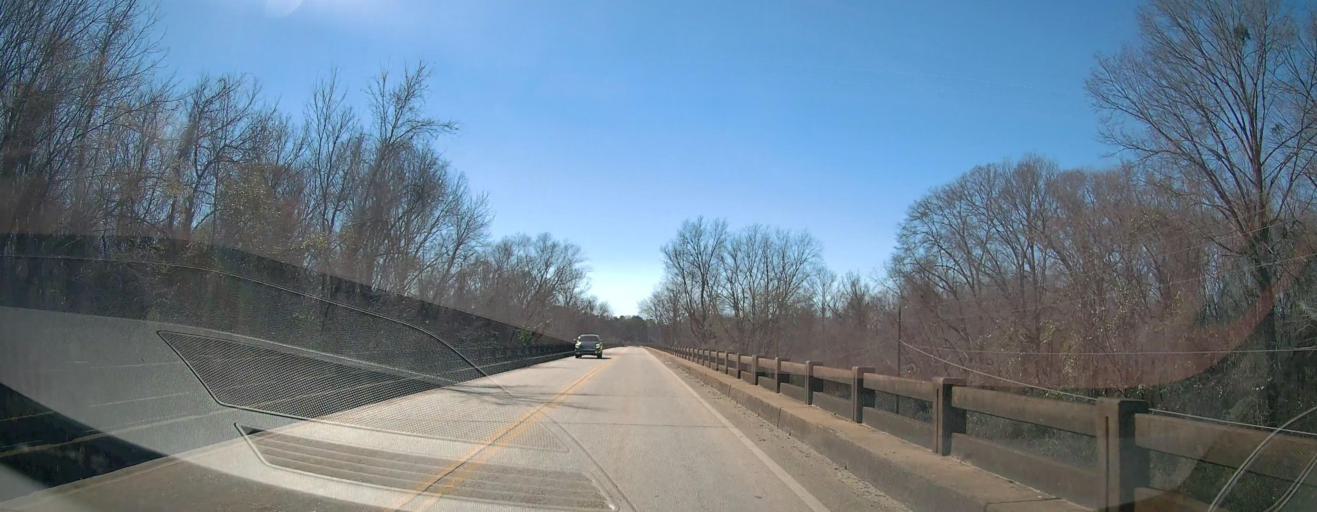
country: US
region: Georgia
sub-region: Macon County
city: Montezuma
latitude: 32.2983
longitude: -84.0425
